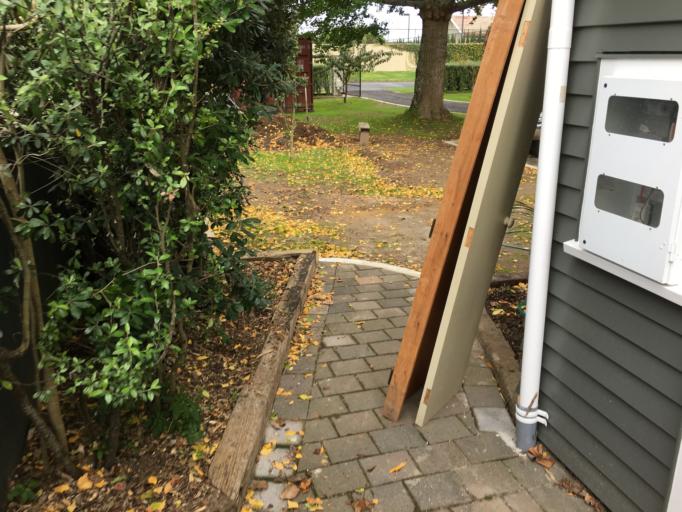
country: NZ
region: Waikato
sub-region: Hamilton City
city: Hamilton
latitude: -37.7742
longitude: 175.2774
